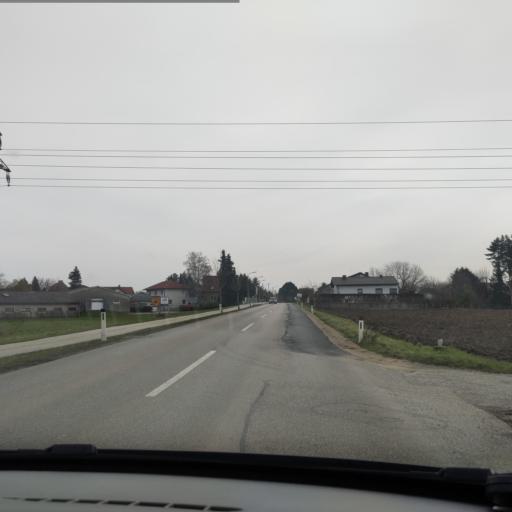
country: AT
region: Lower Austria
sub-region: Sankt Polten Stadt
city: Sankt Poelten
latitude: 48.2192
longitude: 15.5994
